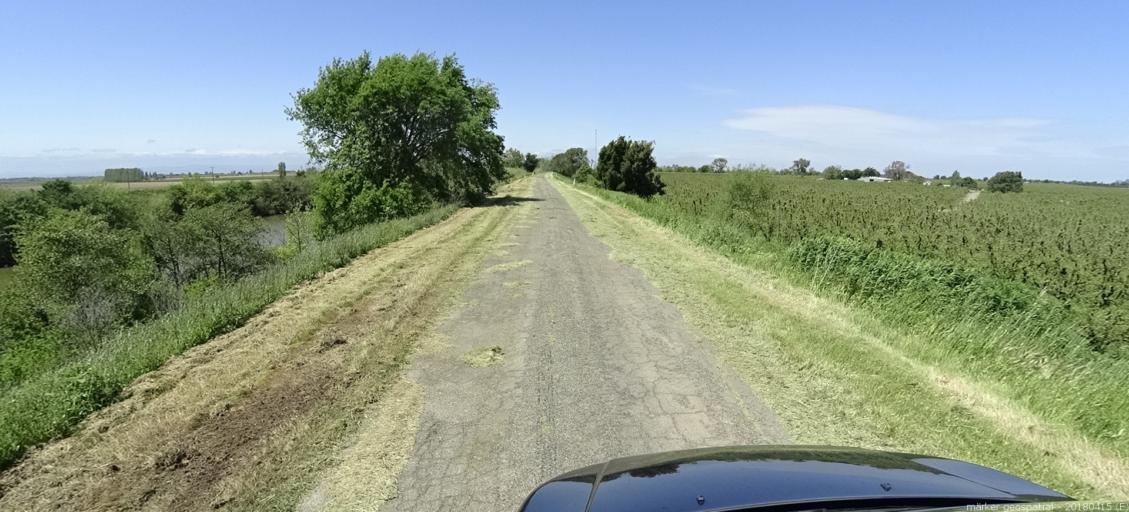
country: US
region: California
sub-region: Sacramento County
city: Walnut Grove
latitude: 38.2824
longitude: -121.6017
